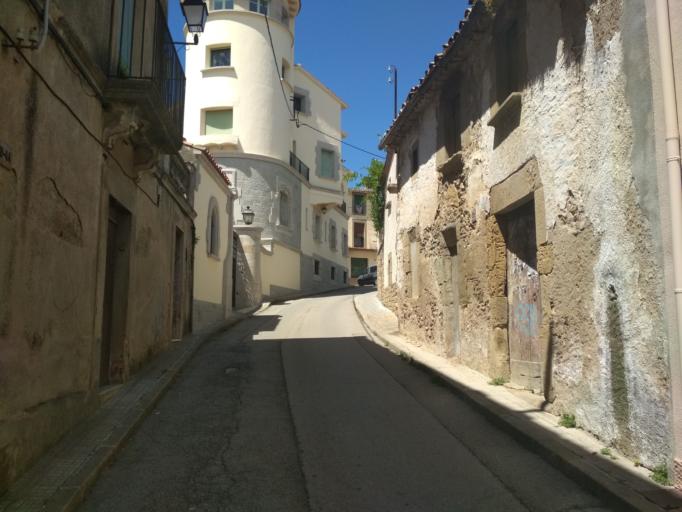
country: ES
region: Catalonia
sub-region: Provincia de Barcelona
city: Castelltercol
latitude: 41.7508
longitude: 2.1220
